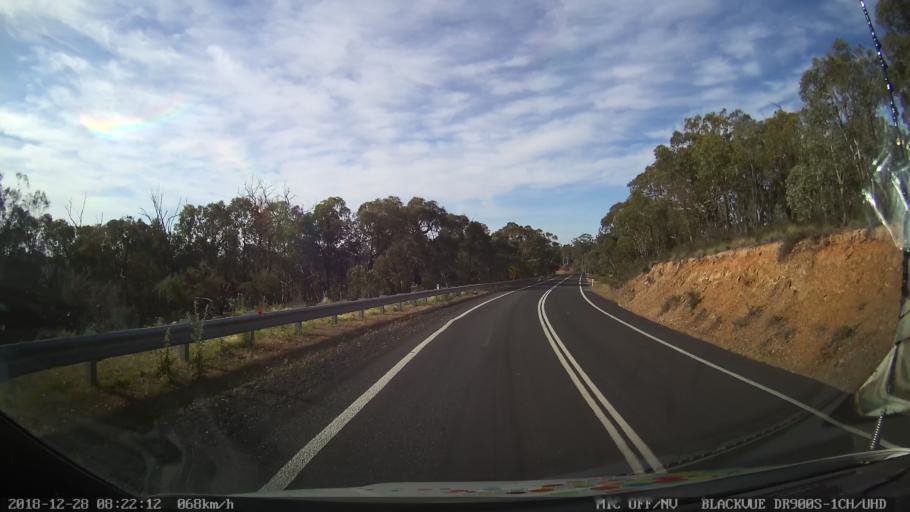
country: AU
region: New South Wales
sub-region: Blayney
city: Blayney
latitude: -33.8910
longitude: 149.3490
